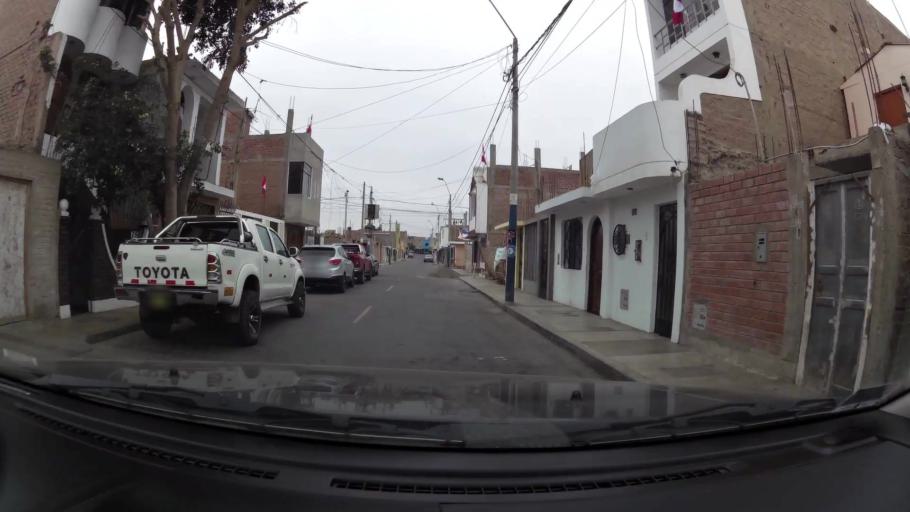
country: PE
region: Ica
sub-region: Provincia de Pisco
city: Pisco
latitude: -13.7124
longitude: -76.2001
